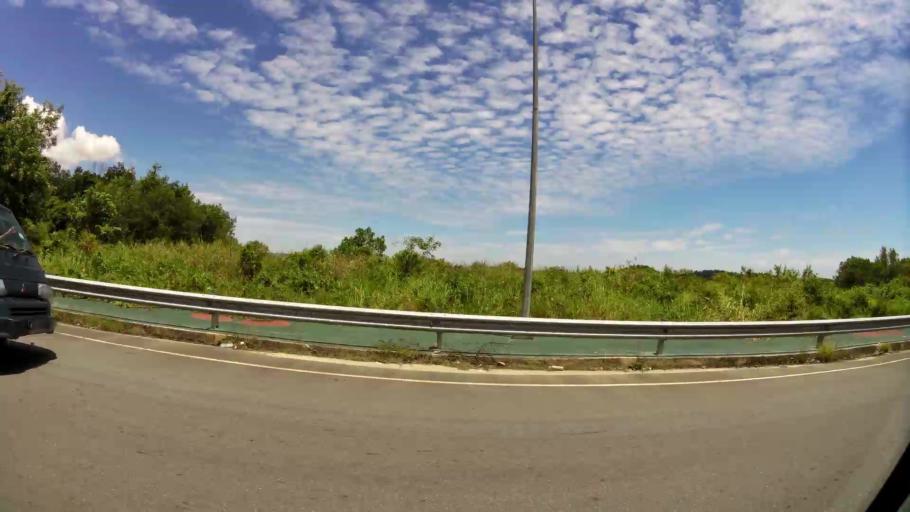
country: BN
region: Brunei and Muara
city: Bandar Seri Begawan
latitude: 5.0036
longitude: 115.0121
